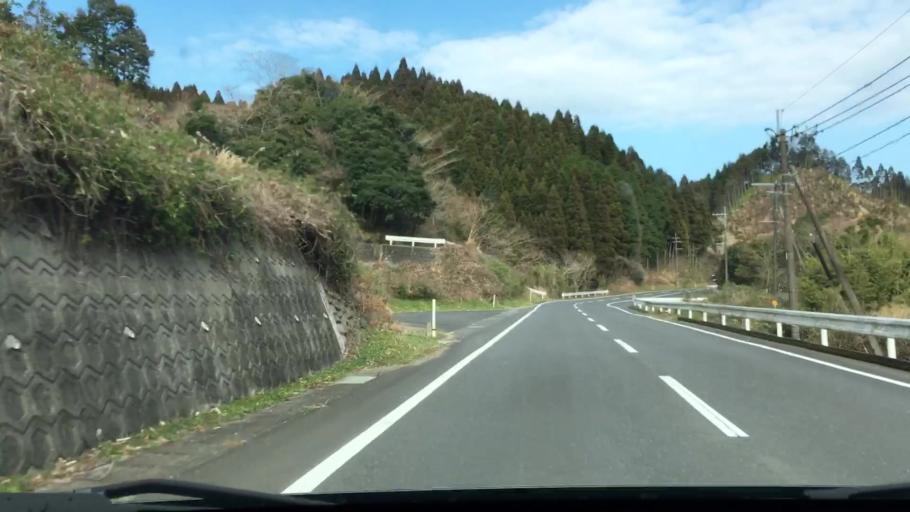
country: JP
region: Miyazaki
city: Kushima
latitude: 31.5744
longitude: 131.2663
